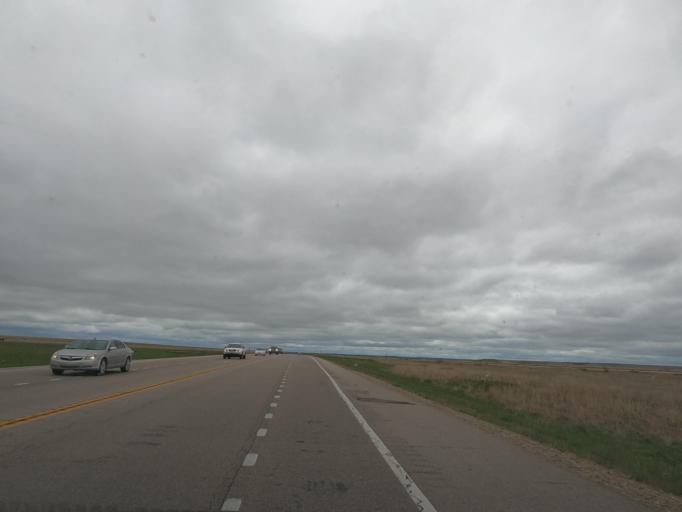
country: US
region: Kansas
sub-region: Greenwood County
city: Eureka
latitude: 37.6437
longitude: -96.4377
